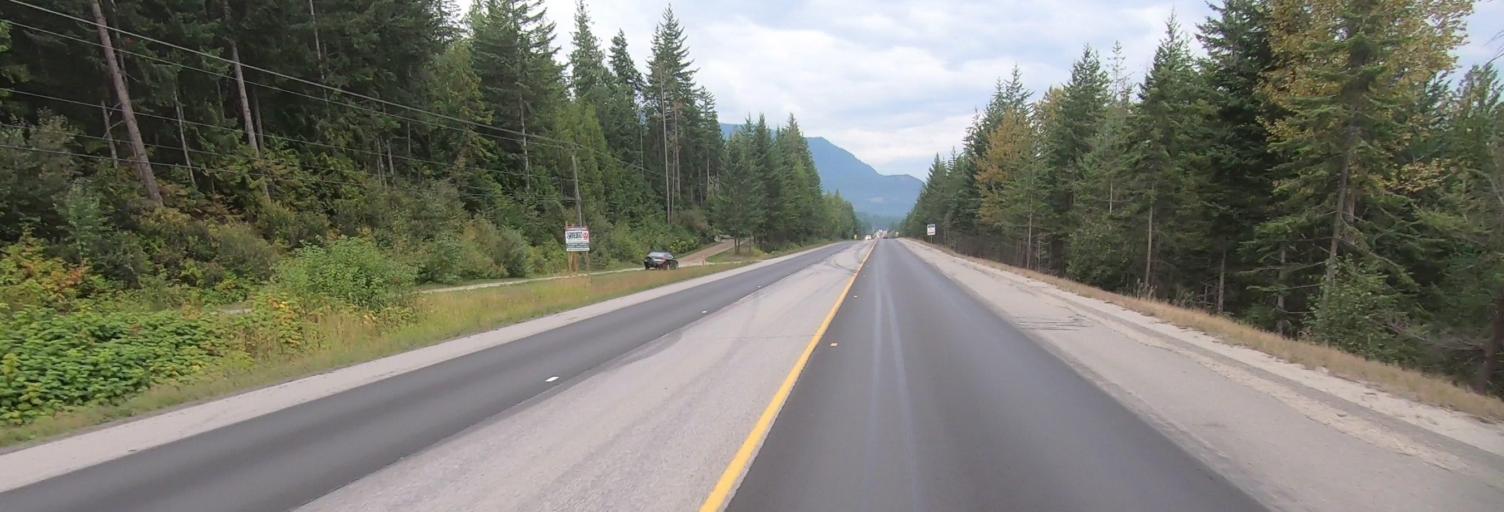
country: CA
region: British Columbia
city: Salmon Arm
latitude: 50.8770
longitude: -119.4430
